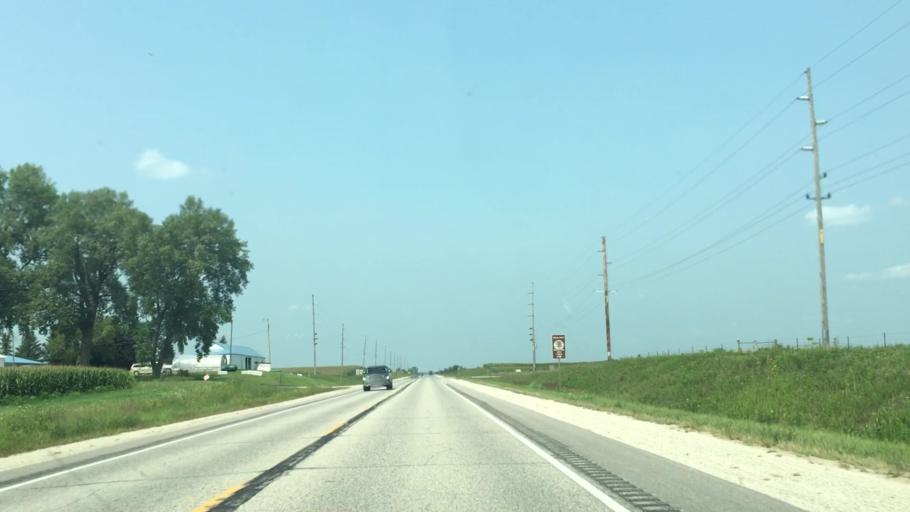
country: US
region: Iowa
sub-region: Fayette County
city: Fayette
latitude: 42.8819
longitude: -91.8105
